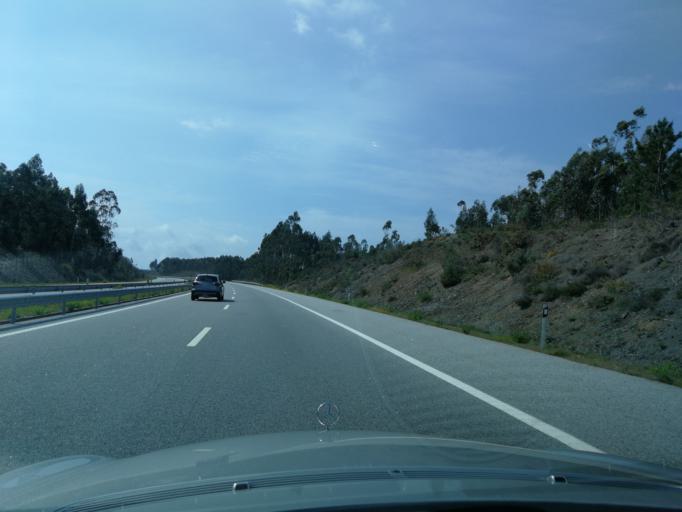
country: PT
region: Braga
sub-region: Vila Nova de Famalicao
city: Ribeirao
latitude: 41.3935
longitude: -8.5979
